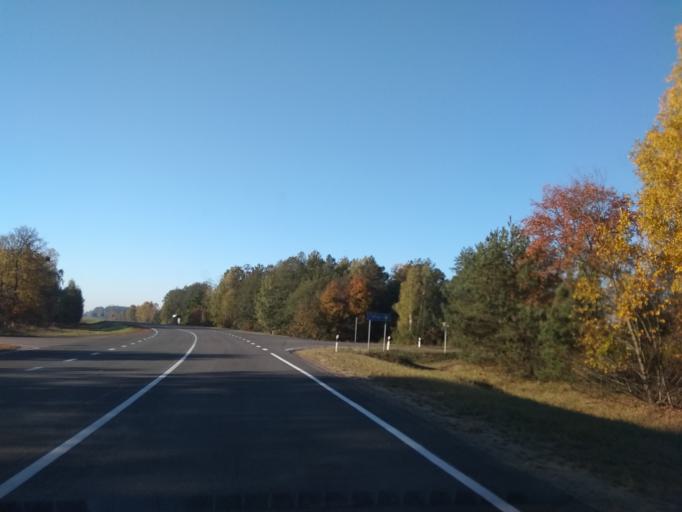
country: BY
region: Brest
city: Kobryn
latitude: 52.0080
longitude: 24.2180
